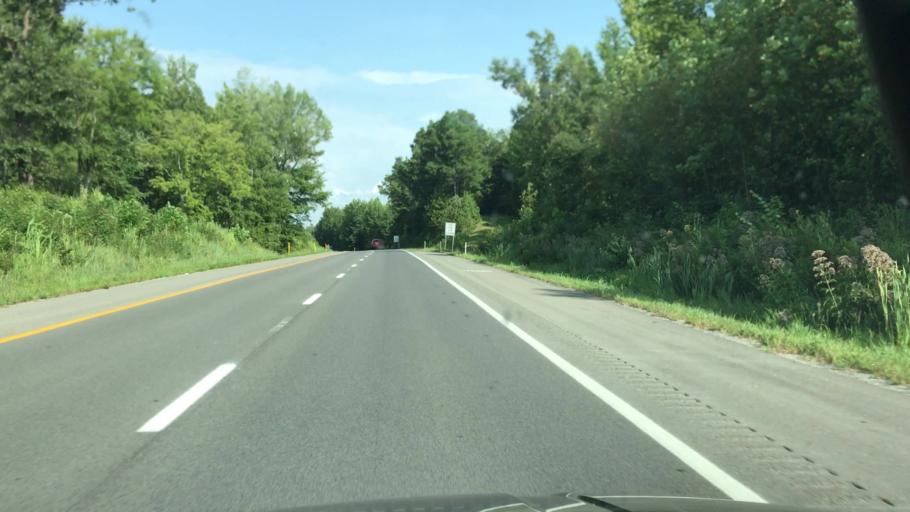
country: US
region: Kentucky
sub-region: Hopkins County
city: Nortonville
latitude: 37.2114
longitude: -87.4241
